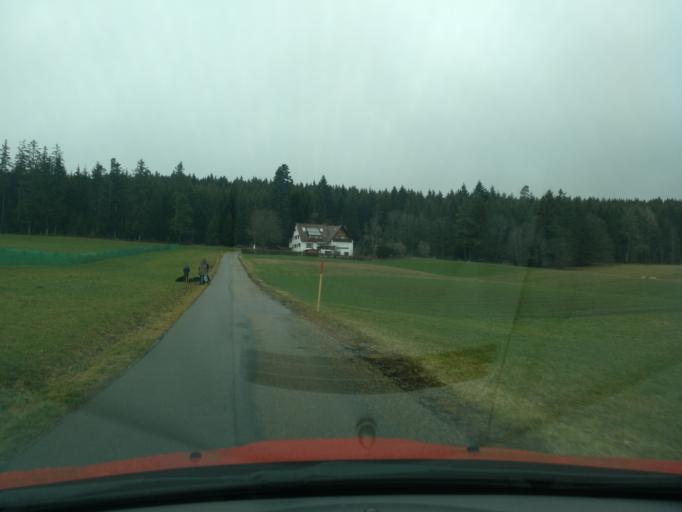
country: DE
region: Baden-Wuerttemberg
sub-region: Freiburg Region
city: Sankt Georgen im Schwarzwald
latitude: 48.1077
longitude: 8.3326
